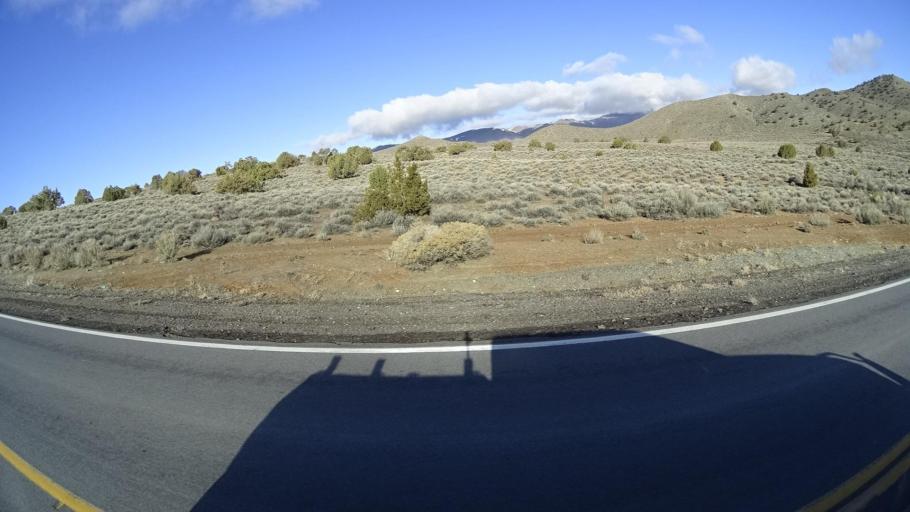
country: US
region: Nevada
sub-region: Washoe County
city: Cold Springs
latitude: 39.6982
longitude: -119.9105
